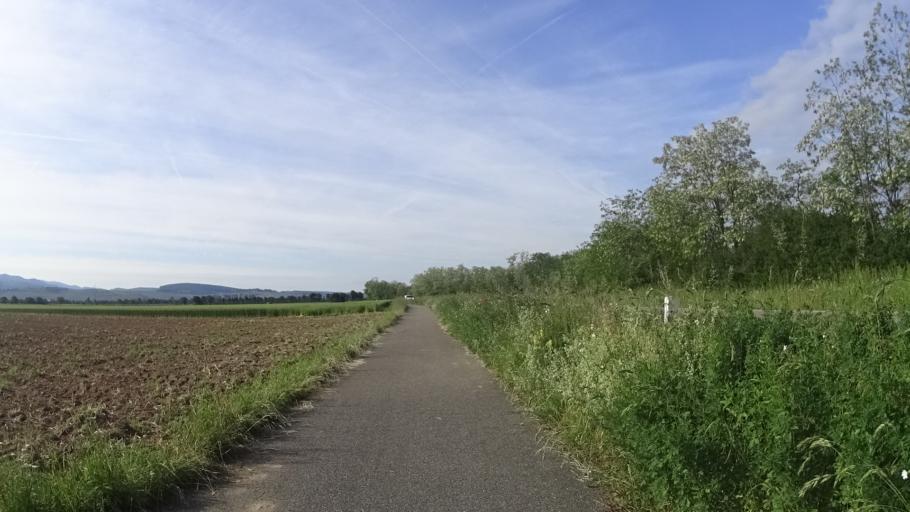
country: DE
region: Baden-Wuerttemberg
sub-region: Freiburg Region
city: Neuenburg am Rhein
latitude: 47.8297
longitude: 7.5742
